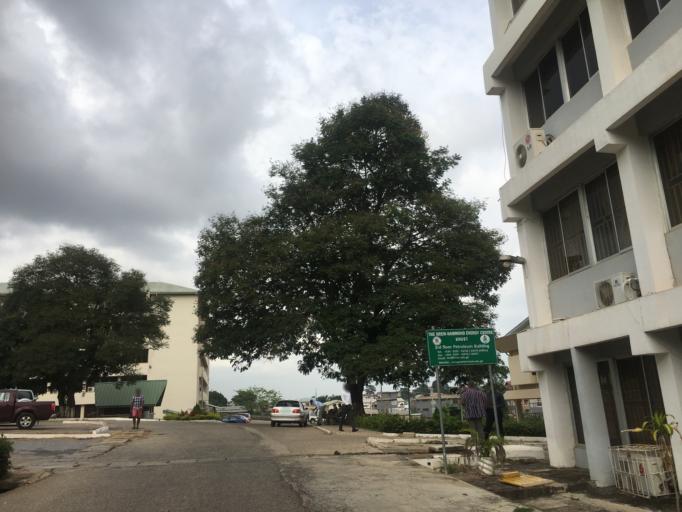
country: GH
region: Ashanti
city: Kumasi
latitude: 6.6730
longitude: -1.5654
